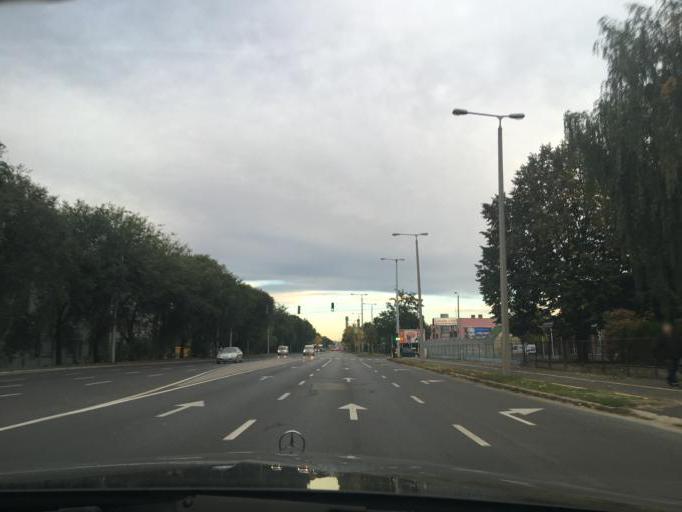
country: HU
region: Hajdu-Bihar
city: Debrecen
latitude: 47.5059
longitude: 21.6305
